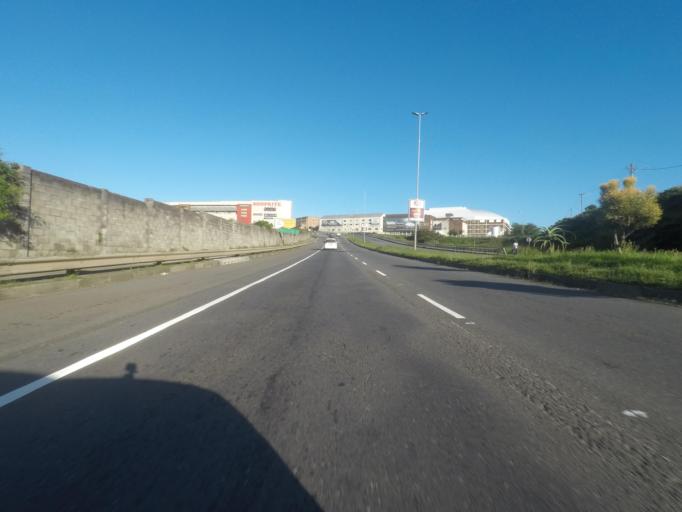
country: ZA
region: Eastern Cape
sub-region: Buffalo City Metropolitan Municipality
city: East London
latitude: -33.0199
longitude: 27.8988
